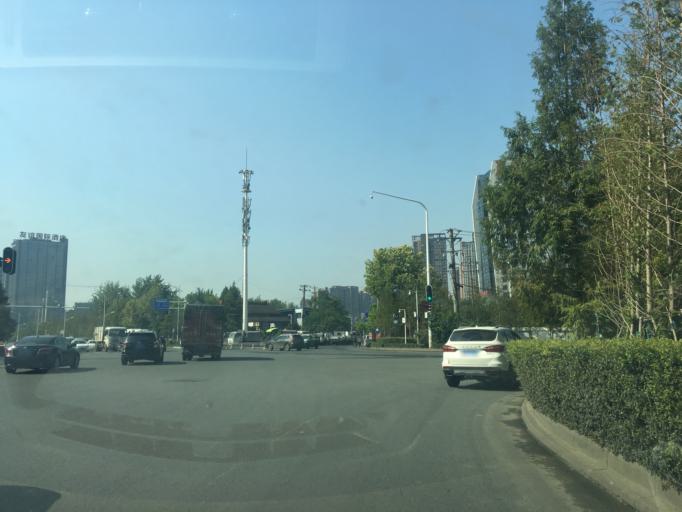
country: CN
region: Hubei
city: Jiang'an
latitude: 30.5686
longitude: 114.3119
